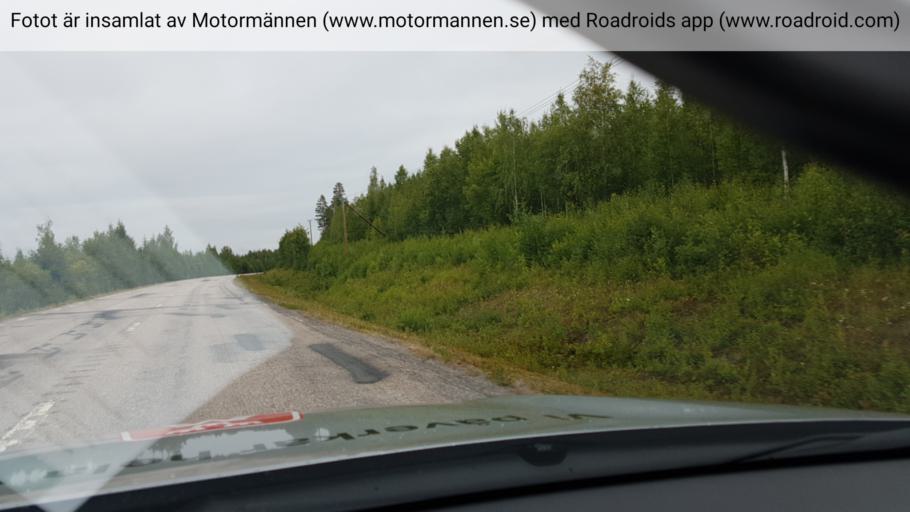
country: SE
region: Norrbotten
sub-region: Alvsbyns Kommun
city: AElvsbyn
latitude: 66.1768
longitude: 20.8781
